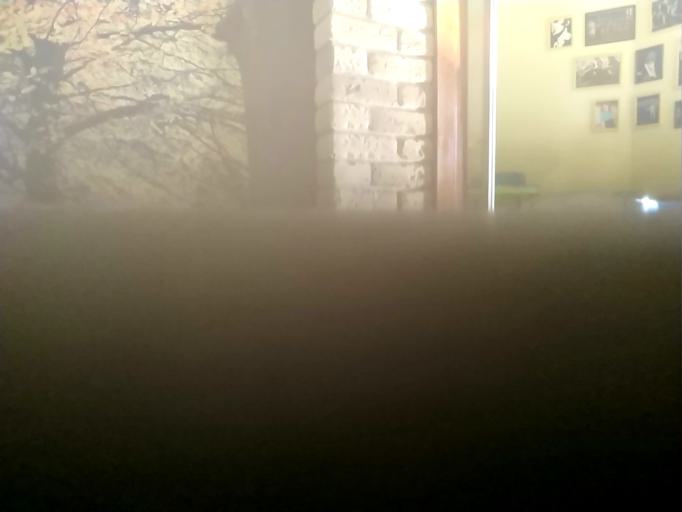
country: RU
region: Smolensk
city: Temkino
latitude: 54.9096
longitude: 34.9720
